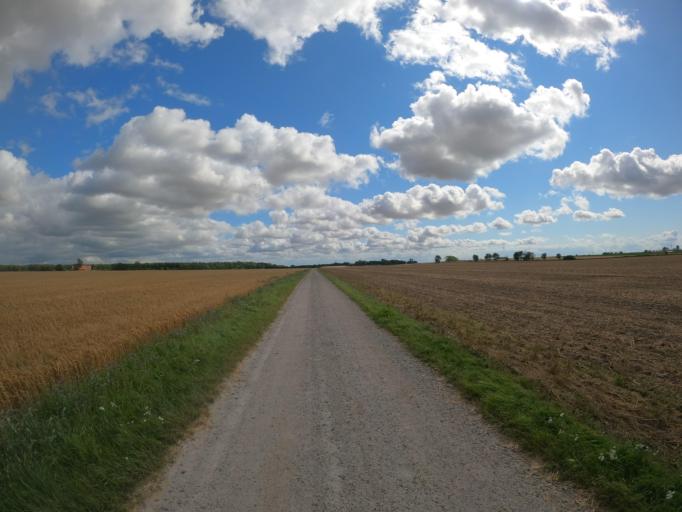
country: SE
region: Skane
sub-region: Lunds Kommun
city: Lund
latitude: 55.7298
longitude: 13.2620
